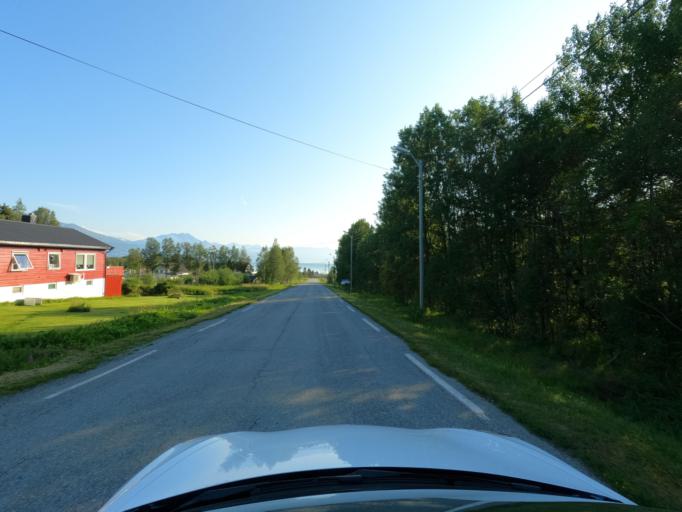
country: NO
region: Nordland
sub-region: Narvik
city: Bjerkvik
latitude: 68.5354
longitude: 17.4816
